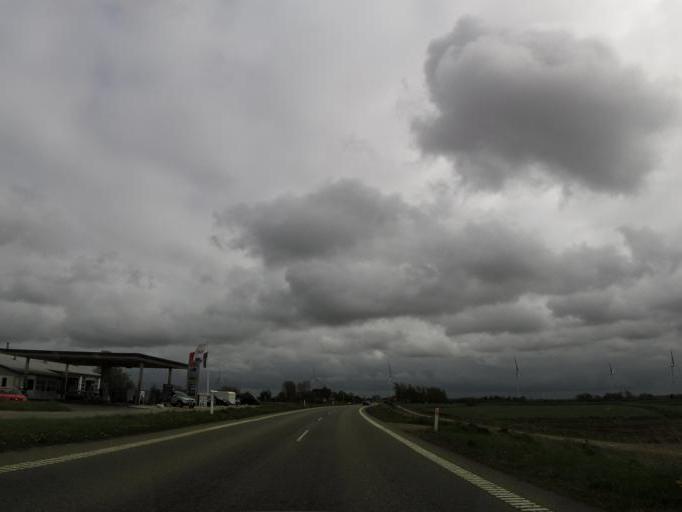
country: DE
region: Schleswig-Holstein
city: Suderlugum
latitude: 54.9100
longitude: 8.9068
